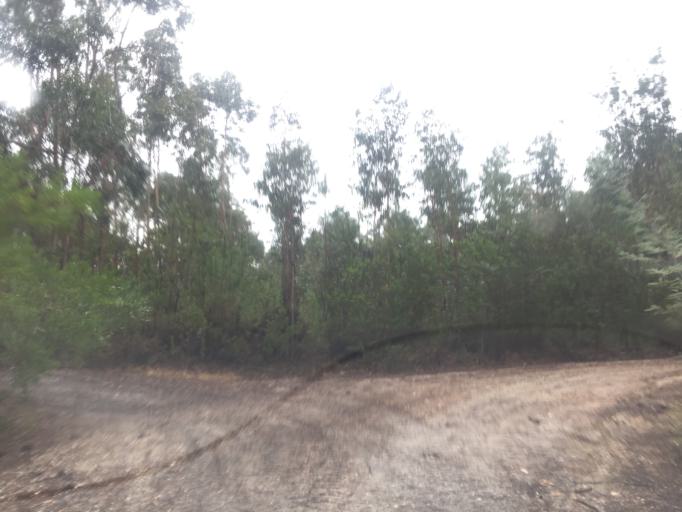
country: PT
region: Coimbra
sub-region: Figueira da Foz
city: Lavos
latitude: 40.0690
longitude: -8.7833
